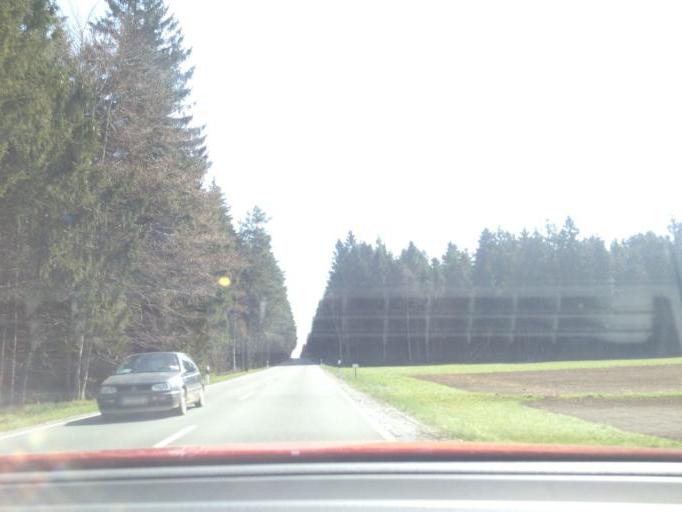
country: DE
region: Bavaria
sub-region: Upper Franconia
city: Oberhaid
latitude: 50.0951
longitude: 11.8048
